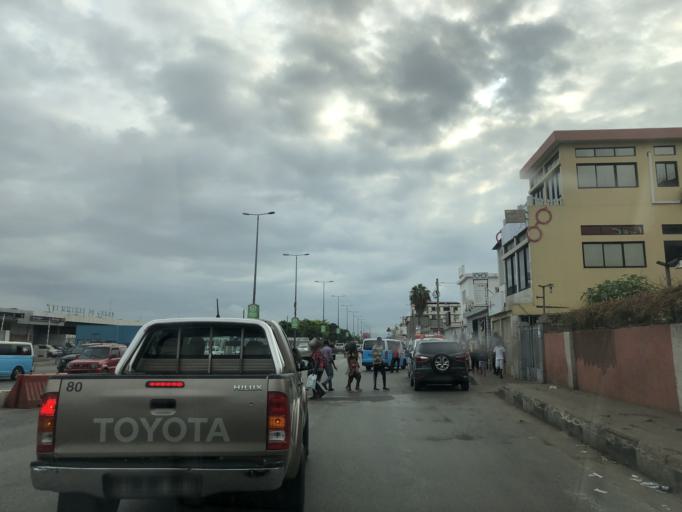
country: AO
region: Luanda
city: Luanda
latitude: -8.8460
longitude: 13.2330
